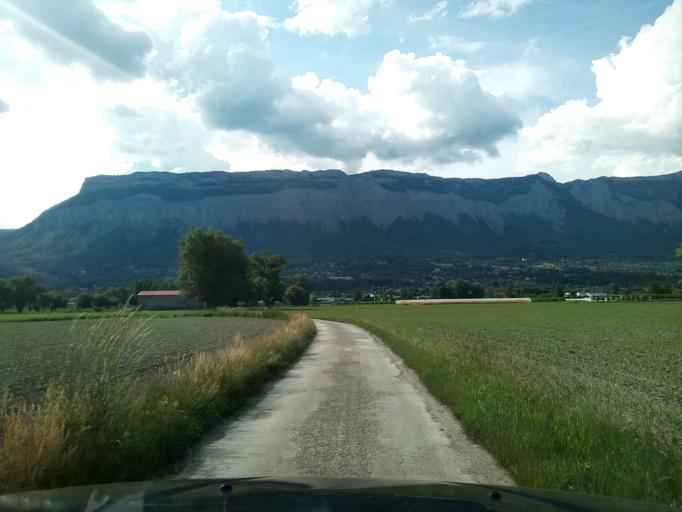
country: FR
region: Rhone-Alpes
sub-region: Departement de l'Isere
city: Domene
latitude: 45.2122
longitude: 5.8213
